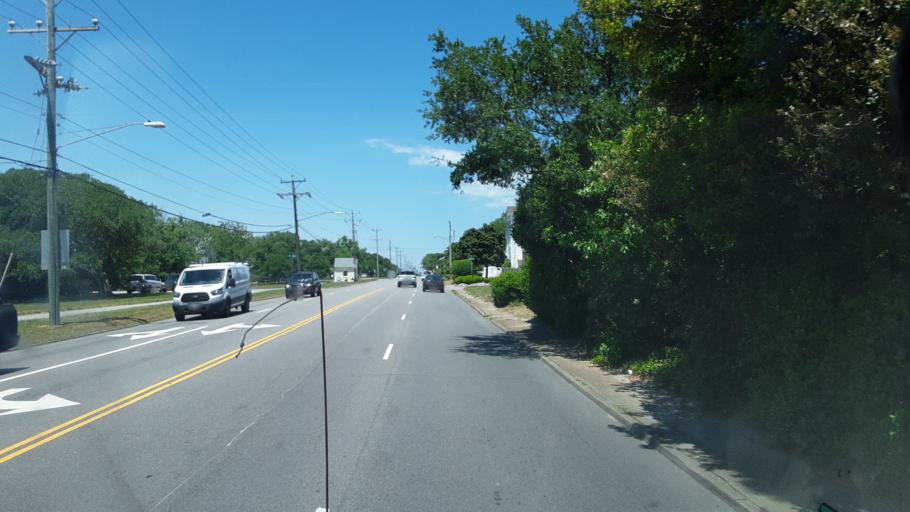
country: US
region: Virginia
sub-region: City of Virginia Beach
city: Virginia Beach
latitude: 36.8750
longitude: -75.9836
